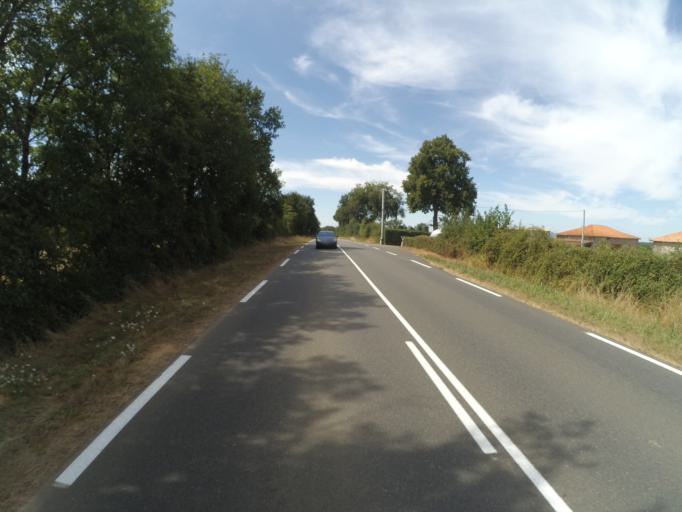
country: FR
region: Poitou-Charentes
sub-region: Departement de la Charente
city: Chabanais
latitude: 45.9500
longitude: 0.7167
